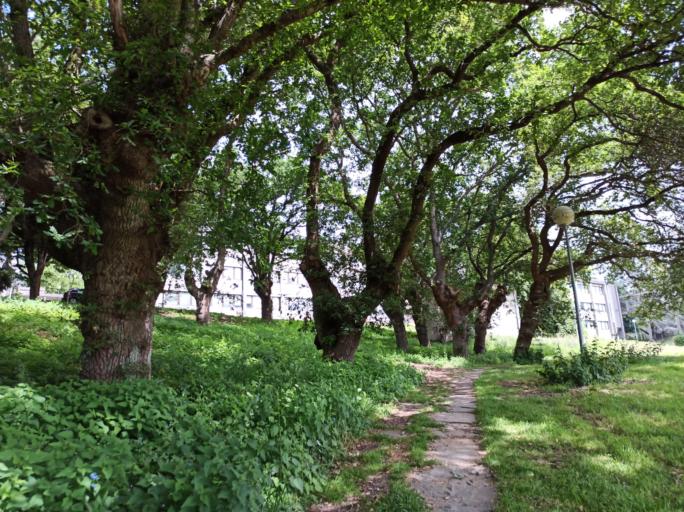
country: ES
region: Galicia
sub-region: Provincia de Lugo
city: Lugo
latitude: 42.9933
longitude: -7.5482
